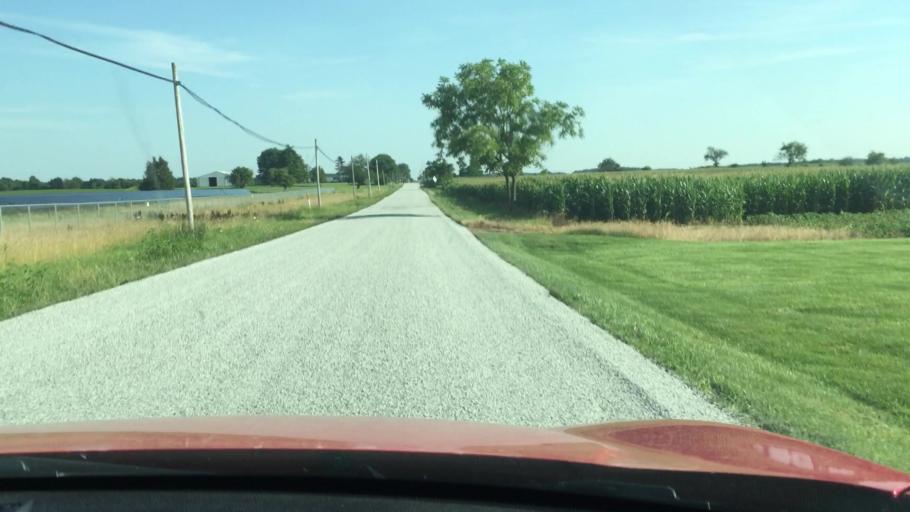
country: US
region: Ohio
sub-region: Hardin County
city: Ada
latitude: 40.7603
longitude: -83.8423
